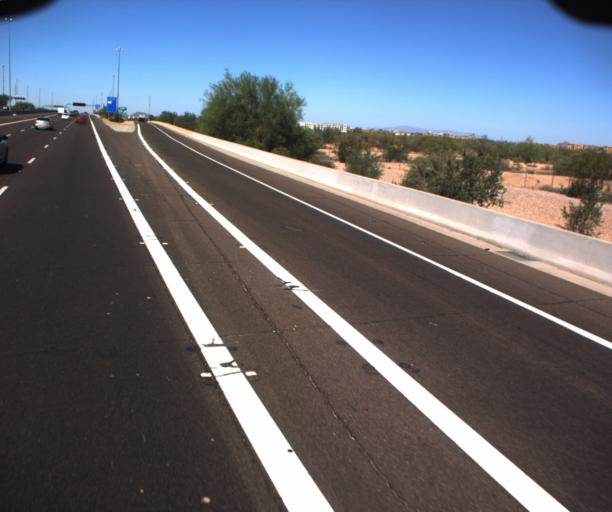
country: US
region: Arizona
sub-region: Maricopa County
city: Paradise Valley
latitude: 33.6654
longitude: -111.9544
